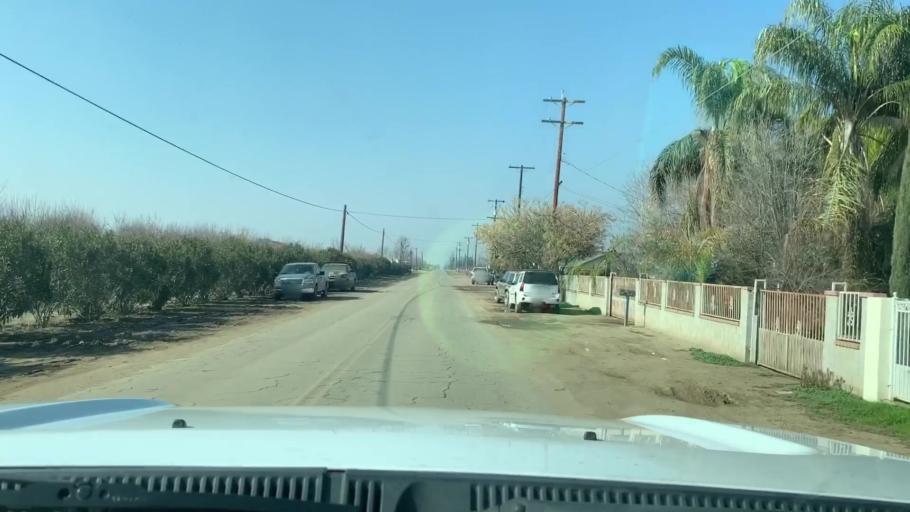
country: US
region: California
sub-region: Kern County
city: Shafter
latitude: 35.4781
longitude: -119.2807
